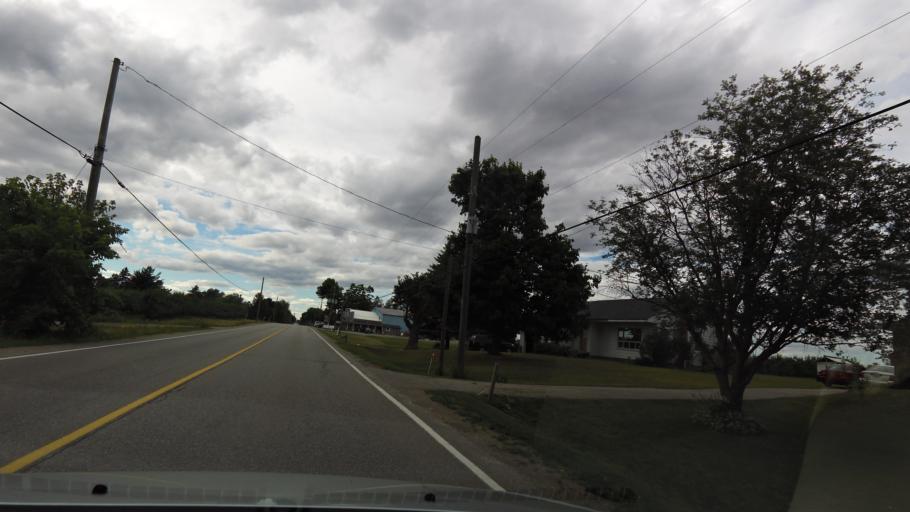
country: CA
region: Ontario
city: Brampton
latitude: 43.6284
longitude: -79.8007
